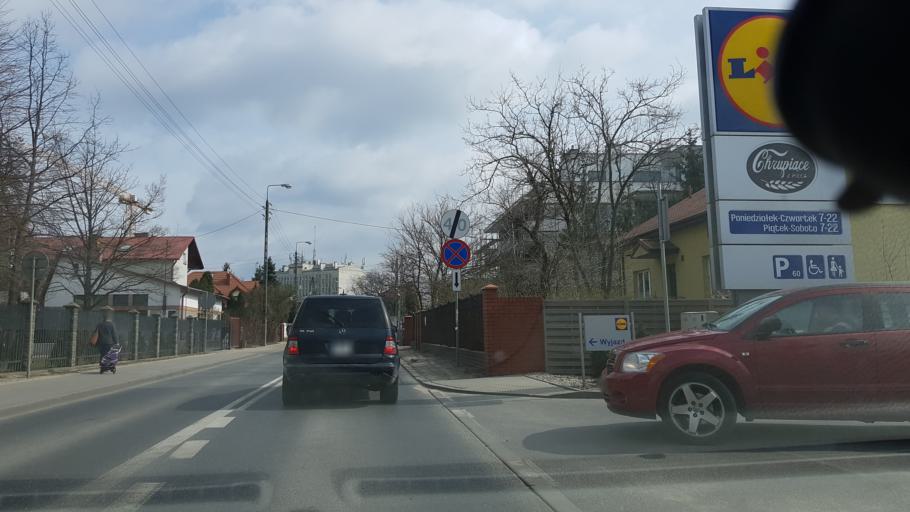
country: PL
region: Masovian Voivodeship
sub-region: Warszawa
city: Rembertow
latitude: 52.2589
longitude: 21.1579
